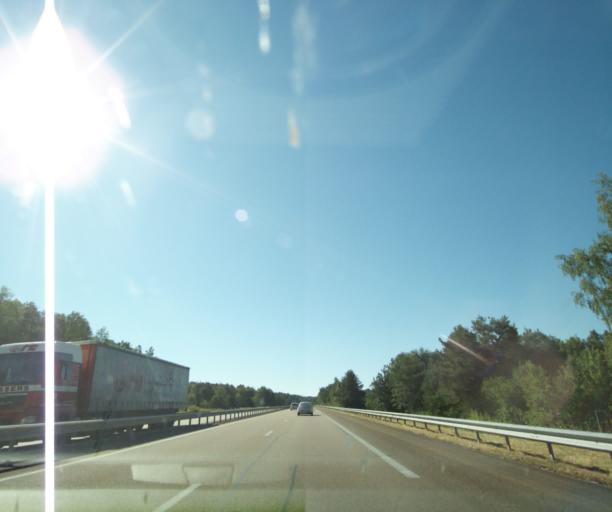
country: FR
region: Champagne-Ardenne
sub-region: Departement de la Haute-Marne
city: Chamarandes-Choignes
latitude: 48.0069
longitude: 5.1078
